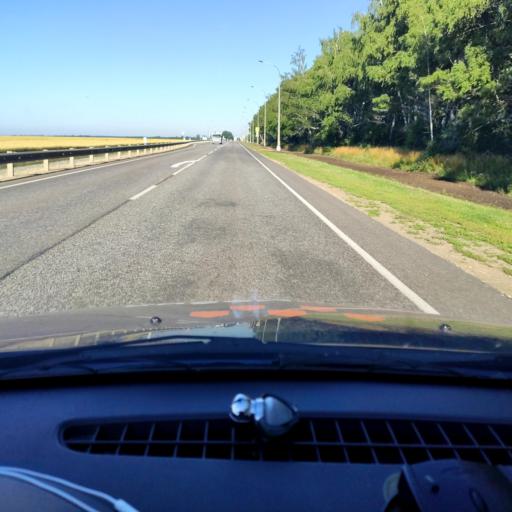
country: RU
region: Orjol
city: Pokrovskoye
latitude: 52.6404
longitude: 36.6555
